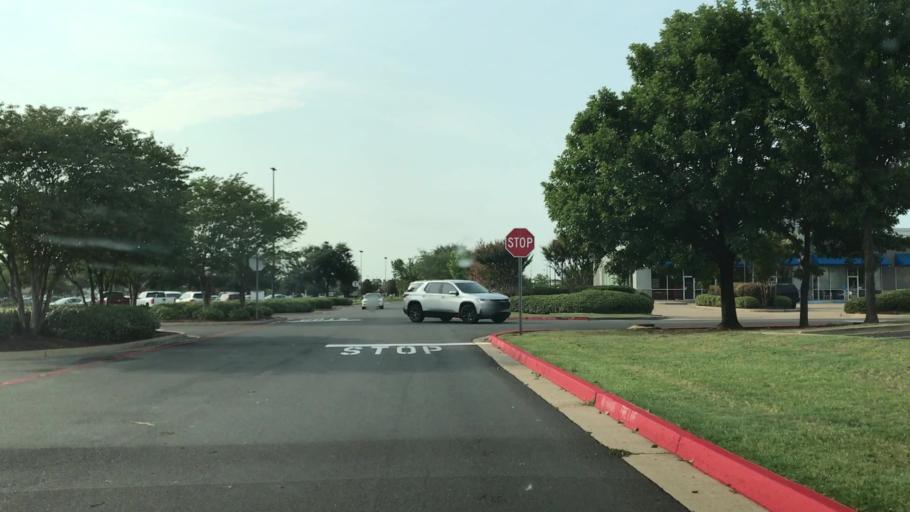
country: US
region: Louisiana
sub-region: Bossier Parish
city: Bossier City
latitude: 32.4384
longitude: -93.7175
